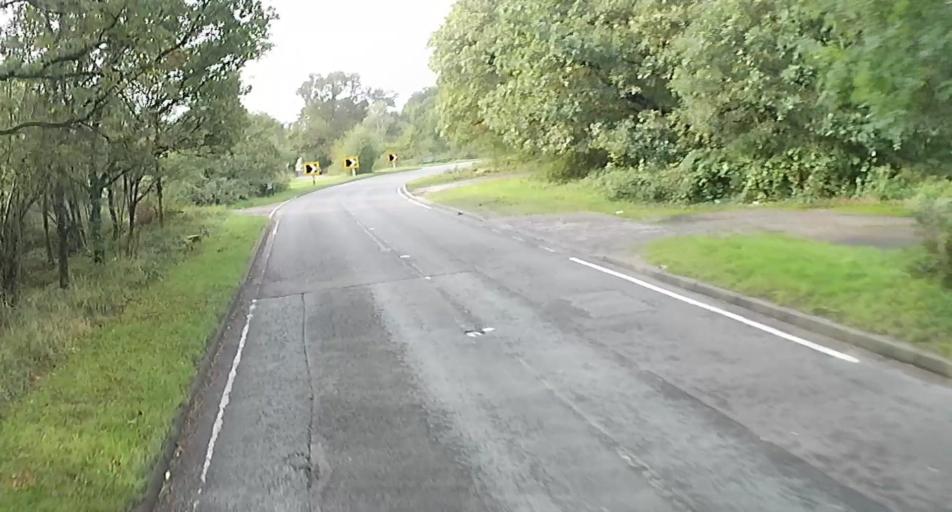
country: GB
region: England
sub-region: West Berkshire
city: Thatcham
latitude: 51.3776
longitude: -1.2476
